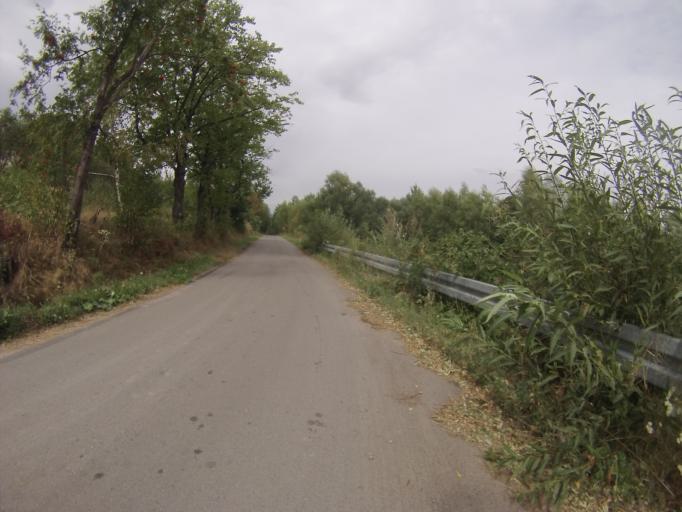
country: PL
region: Swietokrzyskie
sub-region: Powiat kielecki
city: Lagow
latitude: 50.7621
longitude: 21.1064
